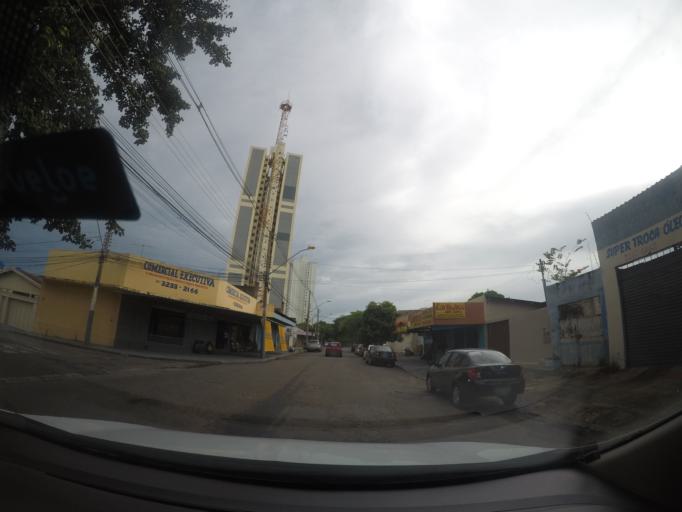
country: BR
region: Goias
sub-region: Goiania
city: Goiania
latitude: -16.6708
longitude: -49.2780
